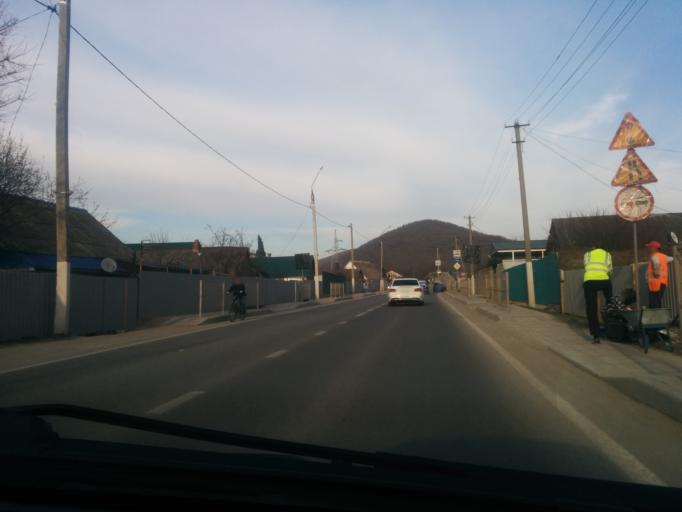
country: RU
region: Krasnodarskiy
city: Novomikhaylovskiy
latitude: 44.2573
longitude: 38.8566
